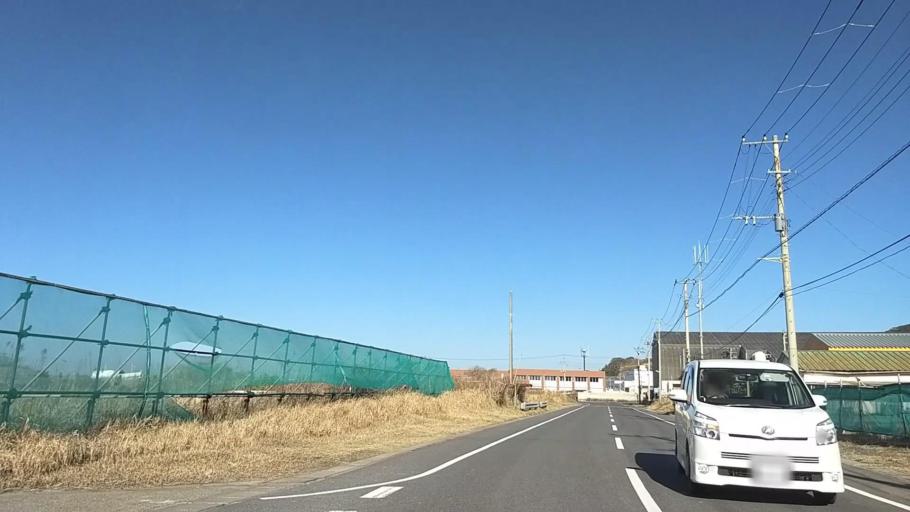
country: JP
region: Chiba
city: Hasaki
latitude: 35.6989
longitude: 140.8473
